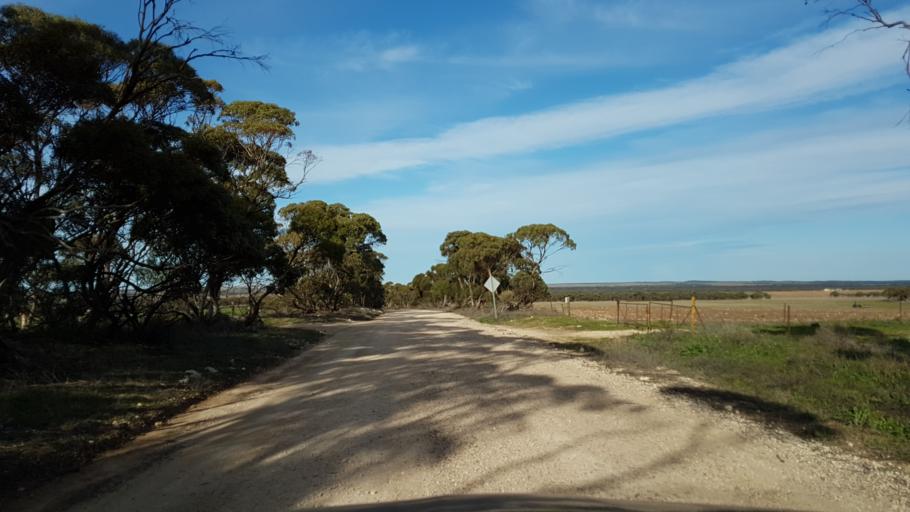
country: AU
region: South Australia
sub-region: Mid Murray
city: Mannum
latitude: -34.9781
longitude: 139.5759
